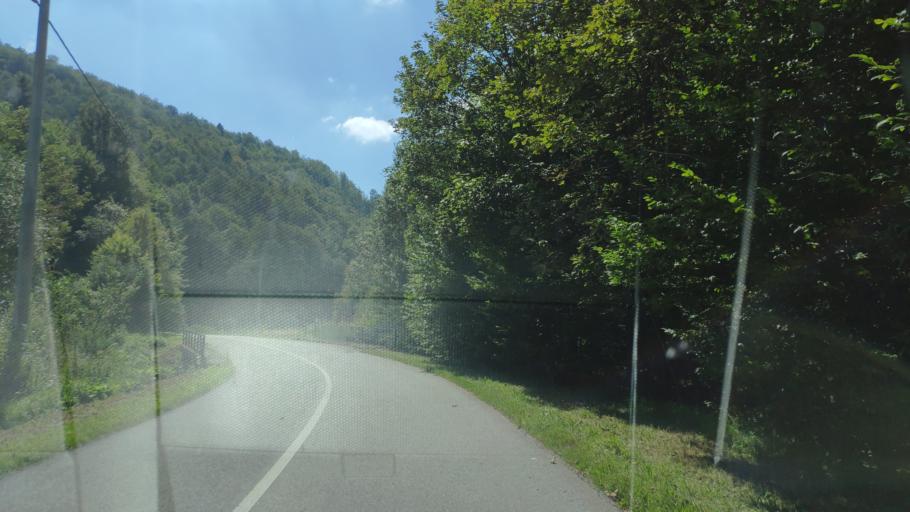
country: PL
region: Subcarpathian Voivodeship
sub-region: Powiat leski
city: Cisna
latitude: 49.0731
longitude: 22.3728
